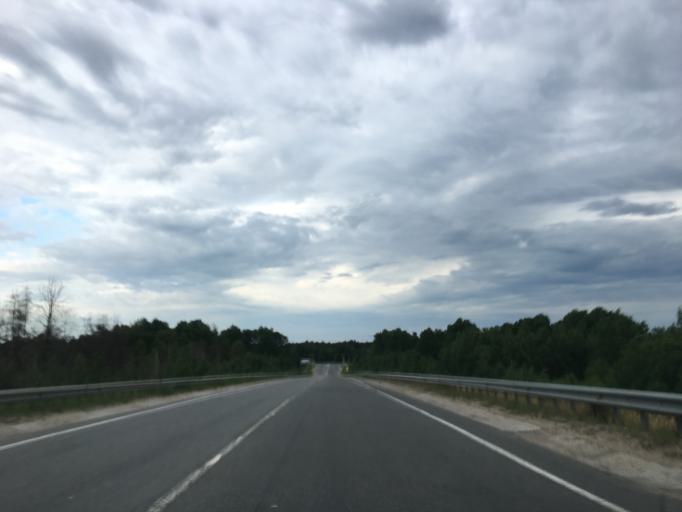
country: RU
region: Pskov
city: Pskov
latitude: 57.8323
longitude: 28.4254
